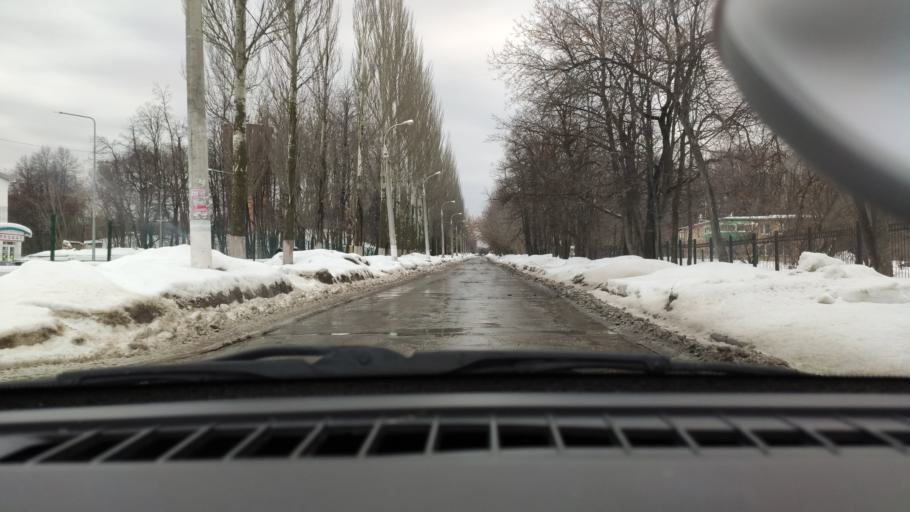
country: RU
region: Samara
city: Petra-Dubrava
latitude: 53.3069
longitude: 50.2776
